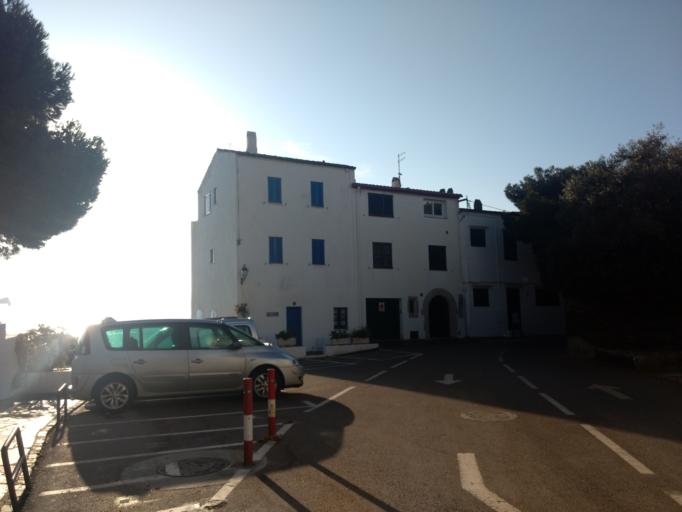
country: ES
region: Catalonia
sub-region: Provincia de Girona
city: Cadaques
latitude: 42.2853
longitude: 3.2756
